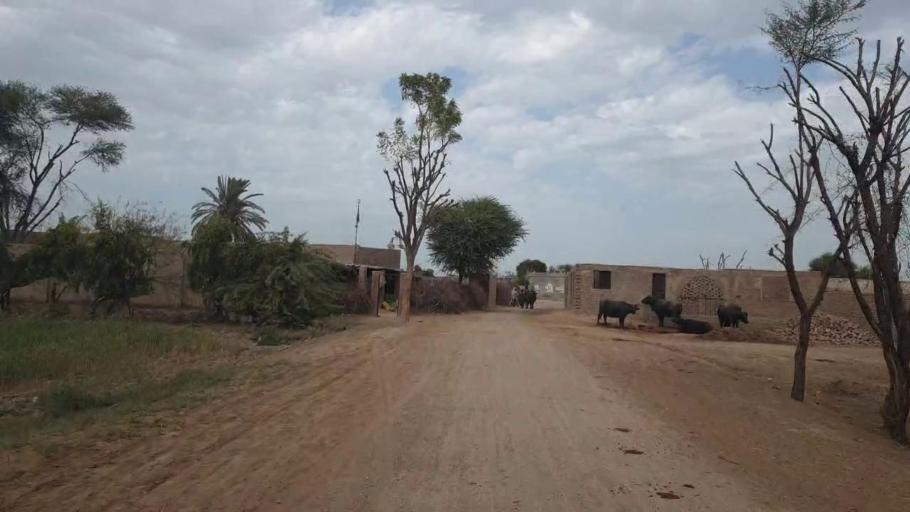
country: PK
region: Sindh
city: Hala
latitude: 25.9381
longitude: 68.4076
